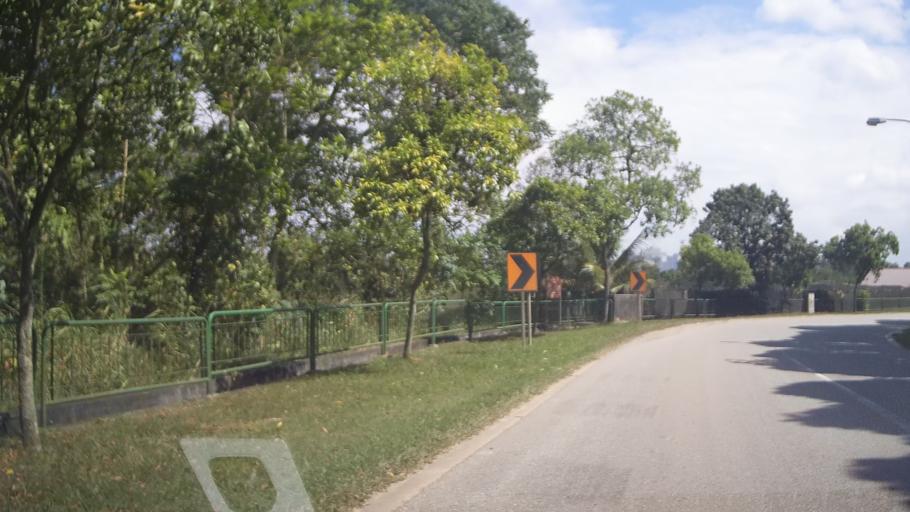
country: MY
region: Johor
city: Johor Bahru
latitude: 1.4300
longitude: 103.7100
